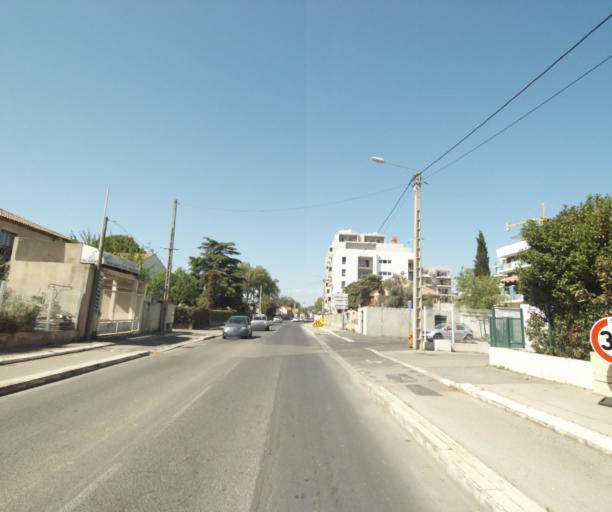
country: FR
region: Languedoc-Roussillon
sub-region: Departement de l'Herault
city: Castelnau-le-Lez
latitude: 43.6169
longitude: 3.8975
